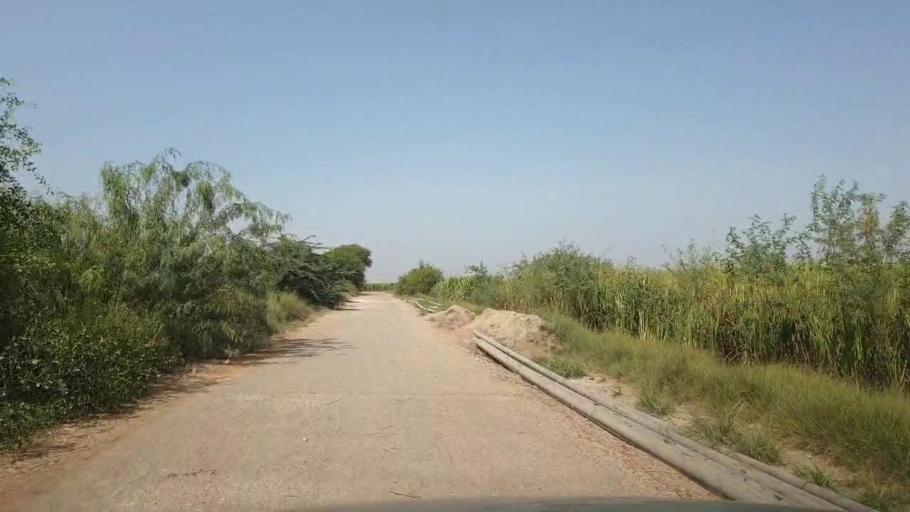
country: PK
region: Sindh
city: Tando Muhammad Khan
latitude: 25.1567
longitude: 68.4049
